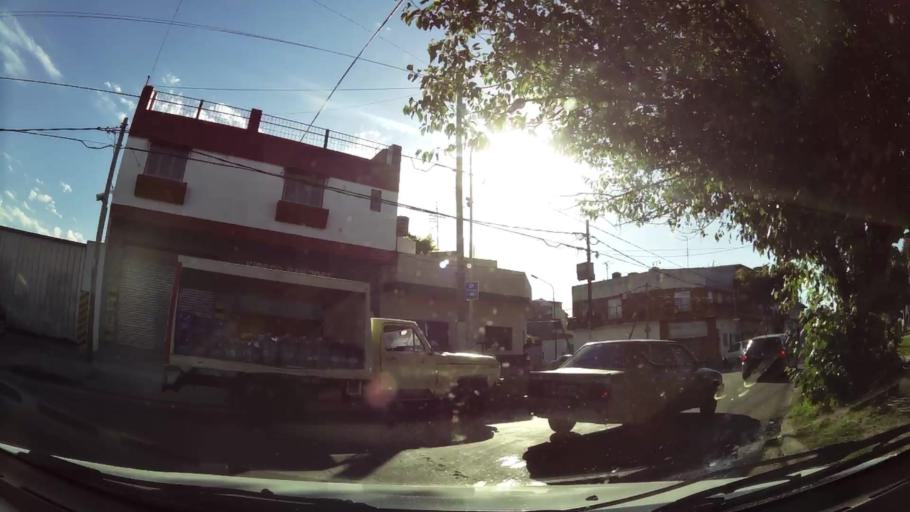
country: AR
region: Buenos Aires
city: Hurlingham
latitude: -34.5636
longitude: -58.6156
